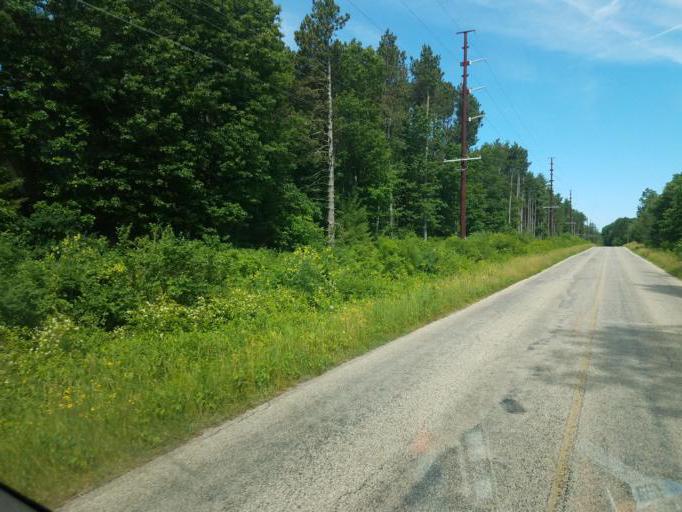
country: US
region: Wisconsin
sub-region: Columbia County
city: Wisconsin Dells
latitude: 43.6719
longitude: -89.7871
